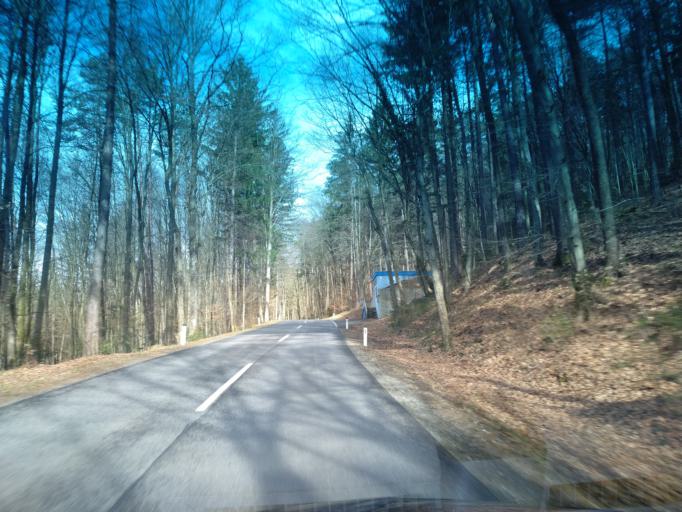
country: AT
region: Styria
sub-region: Politischer Bezirk Leibnitz
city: Kitzeck im Sausal
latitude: 46.7640
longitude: 15.4437
